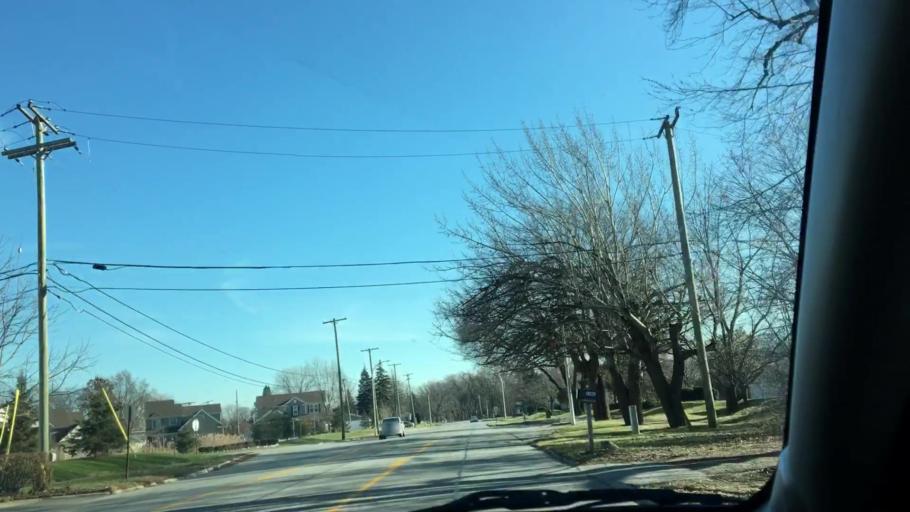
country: US
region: Michigan
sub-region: Wayne County
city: Livonia
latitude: 42.3485
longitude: -83.3682
